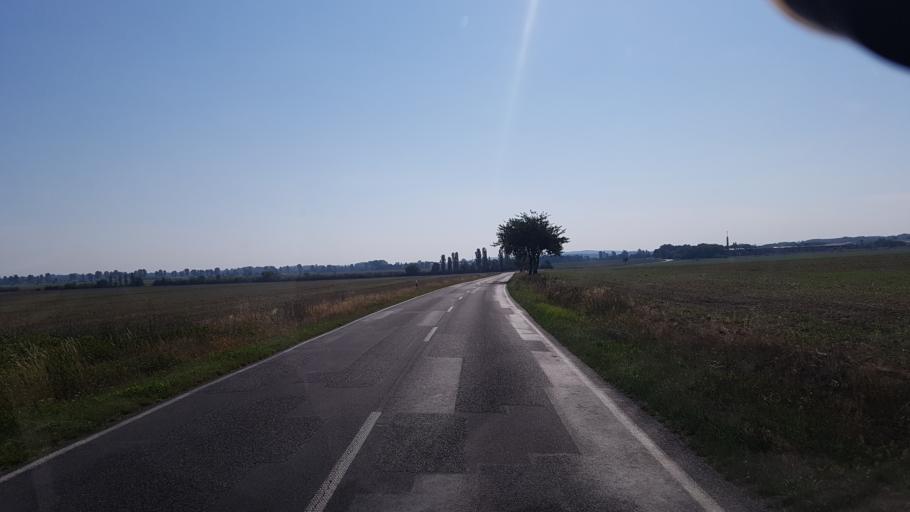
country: DE
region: Brandenburg
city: Groden
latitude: 51.3990
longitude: 13.5919
